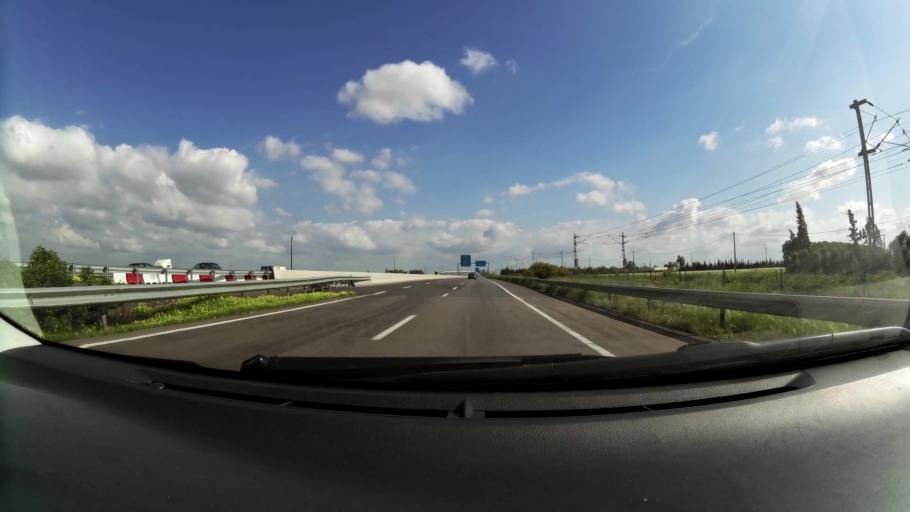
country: MA
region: Chaouia-Ouardigha
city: Nouaseur
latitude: 33.3292
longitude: -7.6082
